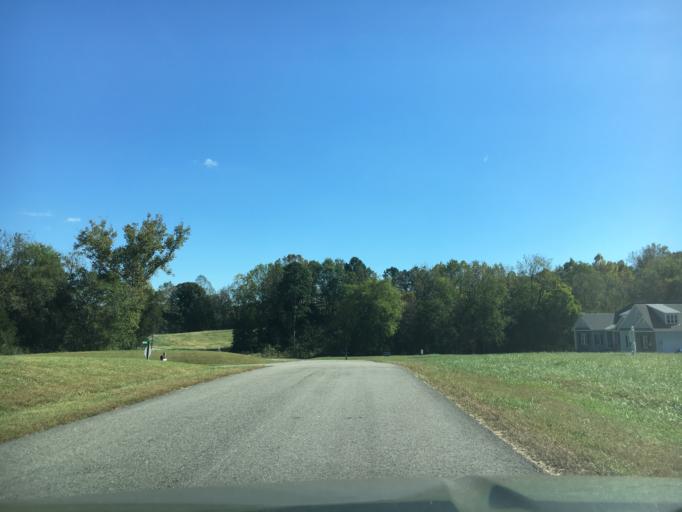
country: US
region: Virginia
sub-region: Goochland County
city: Goochland
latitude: 37.6936
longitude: -77.8358
